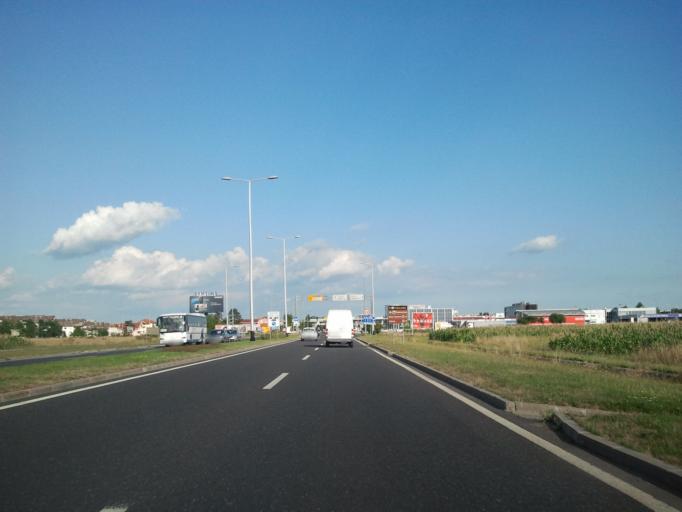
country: HR
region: Zagrebacka
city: Gradici
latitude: 45.7231
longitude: 16.0472
